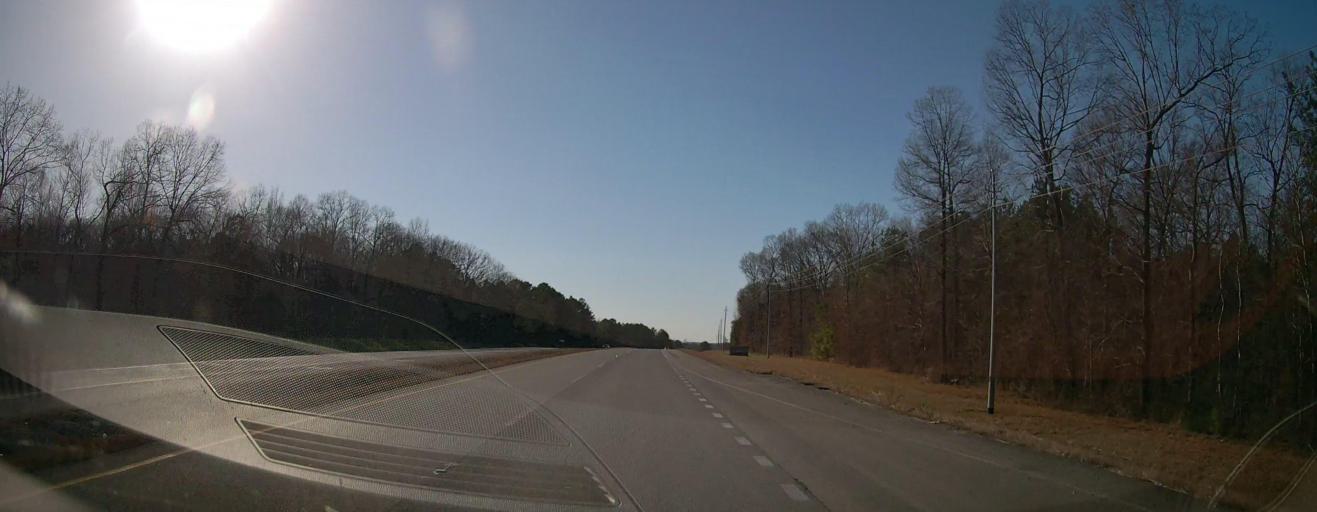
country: US
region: Alabama
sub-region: Colbert County
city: Cherokee
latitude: 34.7473
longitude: -87.9521
